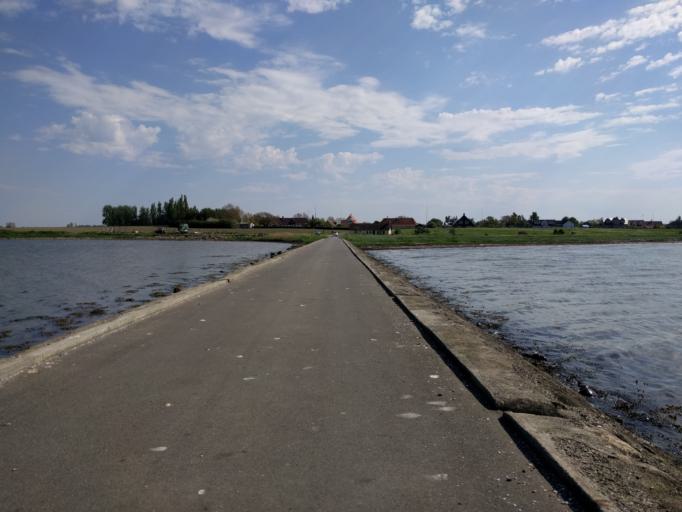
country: DK
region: South Denmark
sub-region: Kerteminde Kommune
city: Munkebo
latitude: 55.4851
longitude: 10.5976
